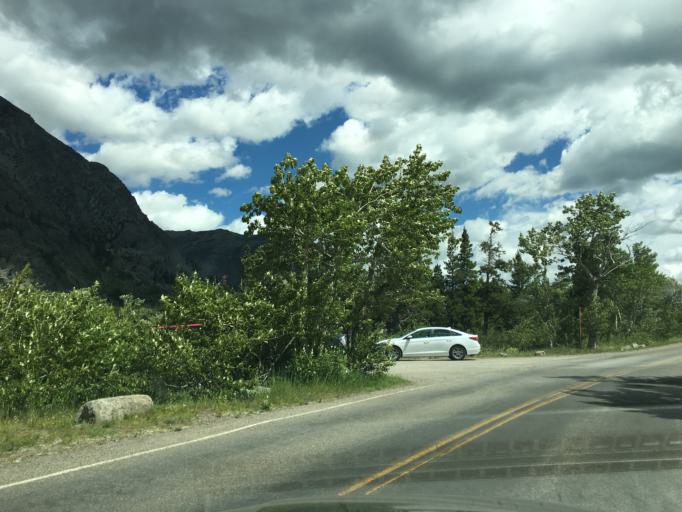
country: US
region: Montana
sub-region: Glacier County
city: South Browning
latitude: 48.4846
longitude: -113.3690
